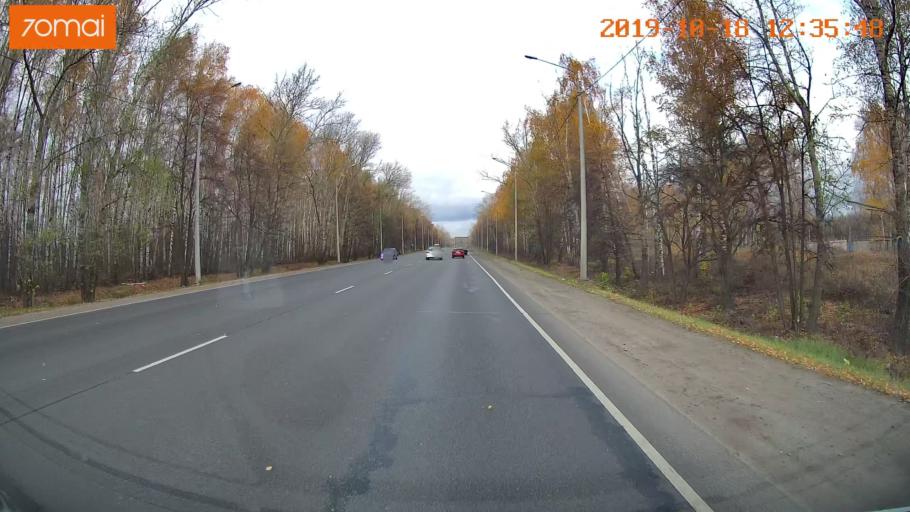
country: RU
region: Rjazan
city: Ryazan'
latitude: 54.6282
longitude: 39.6351
